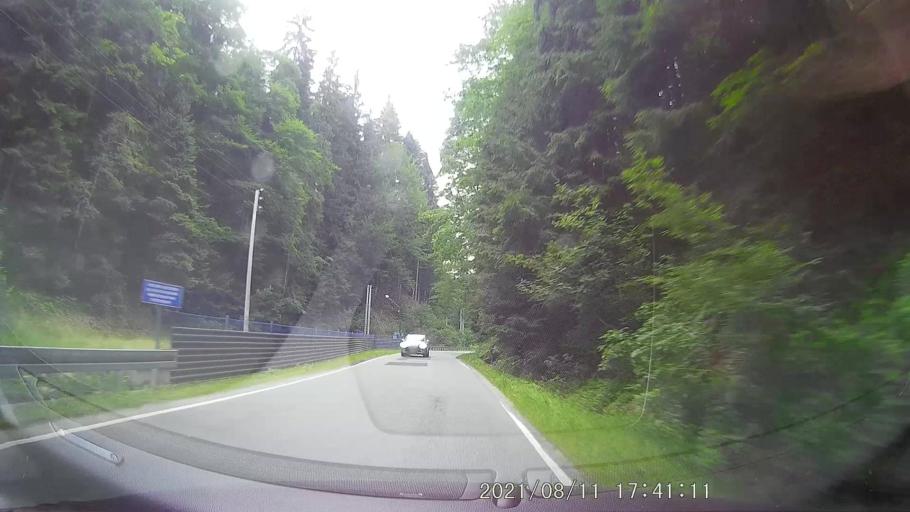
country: PL
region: Lower Silesian Voivodeship
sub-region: Powiat klodzki
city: Duszniki-Zdroj
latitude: 50.3650
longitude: 16.3920
